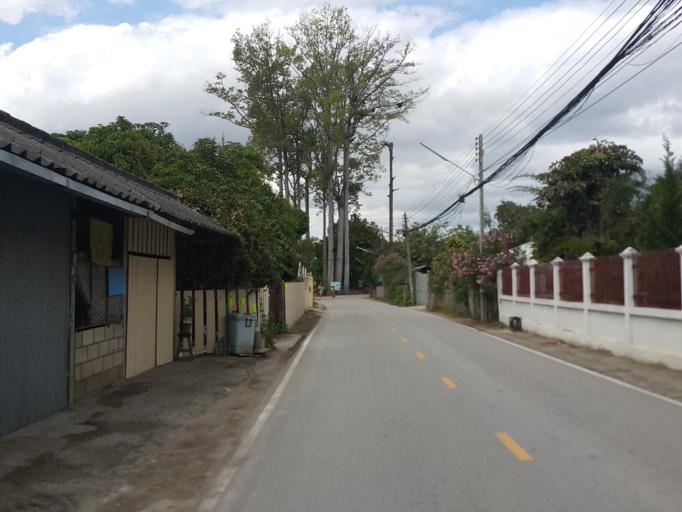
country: TH
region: Chiang Mai
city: San Sai
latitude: 18.8638
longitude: 99.1393
